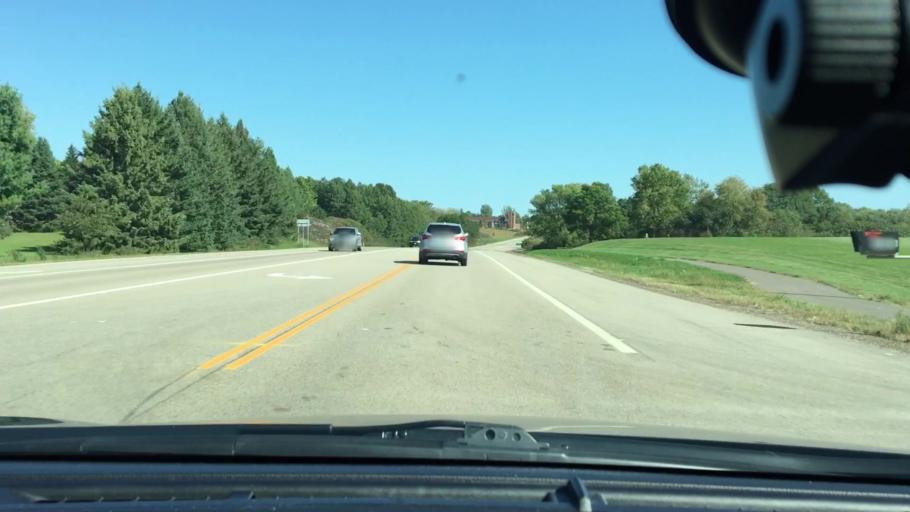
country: US
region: Minnesota
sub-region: Washington County
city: Stillwater
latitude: 45.0586
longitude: -92.8497
